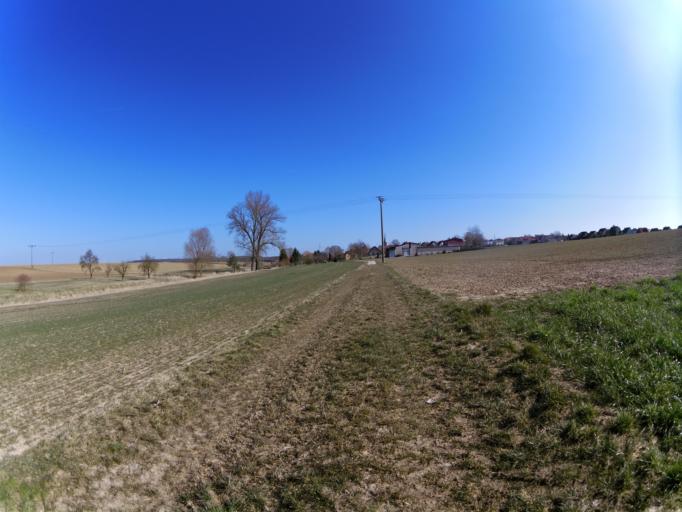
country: DE
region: Bavaria
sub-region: Regierungsbezirk Unterfranken
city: Oberpleichfeld
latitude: 49.8766
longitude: 10.0773
